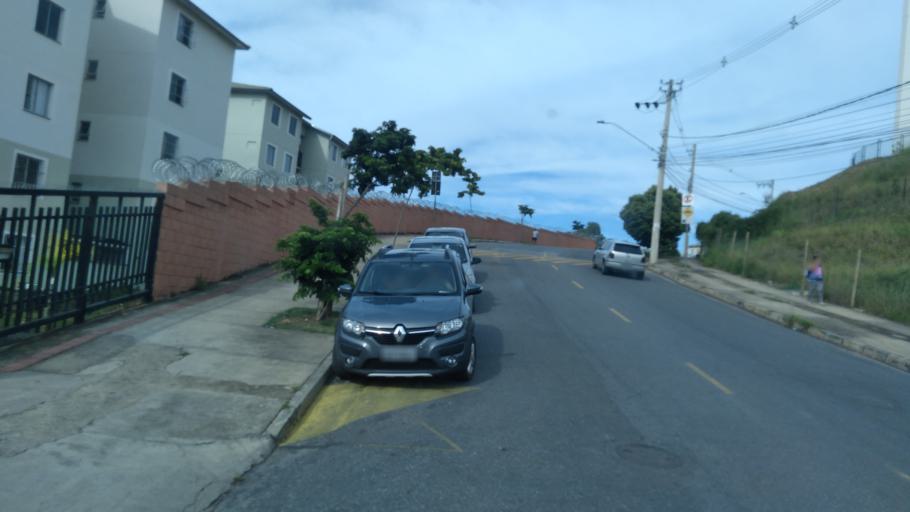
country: BR
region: Minas Gerais
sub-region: Santa Luzia
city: Santa Luzia
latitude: -19.8418
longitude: -43.8914
